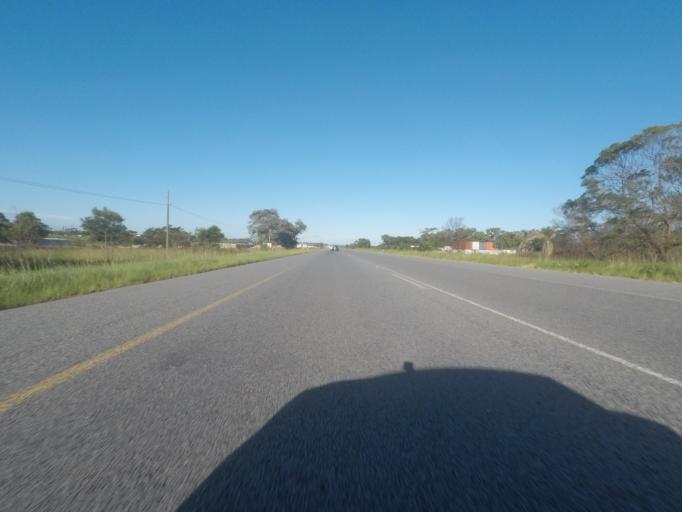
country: ZA
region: Eastern Cape
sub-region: Buffalo City Metropolitan Municipality
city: East London
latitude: -33.0566
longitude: 27.7989
